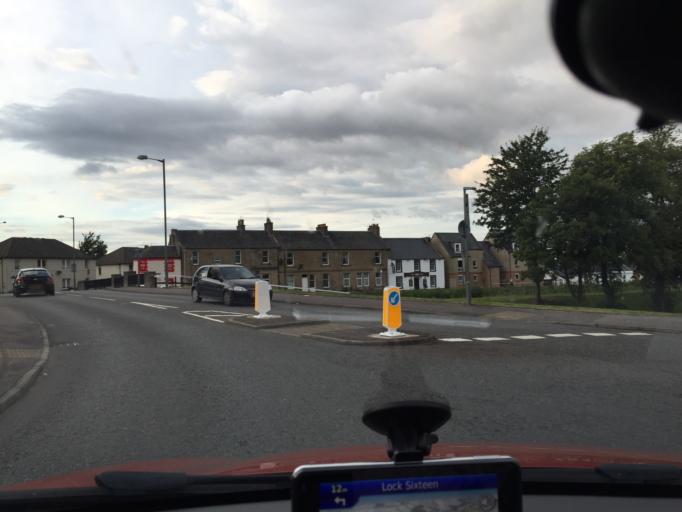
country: GB
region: Scotland
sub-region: Falkirk
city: Larbert
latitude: 55.9995
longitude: -3.8151
